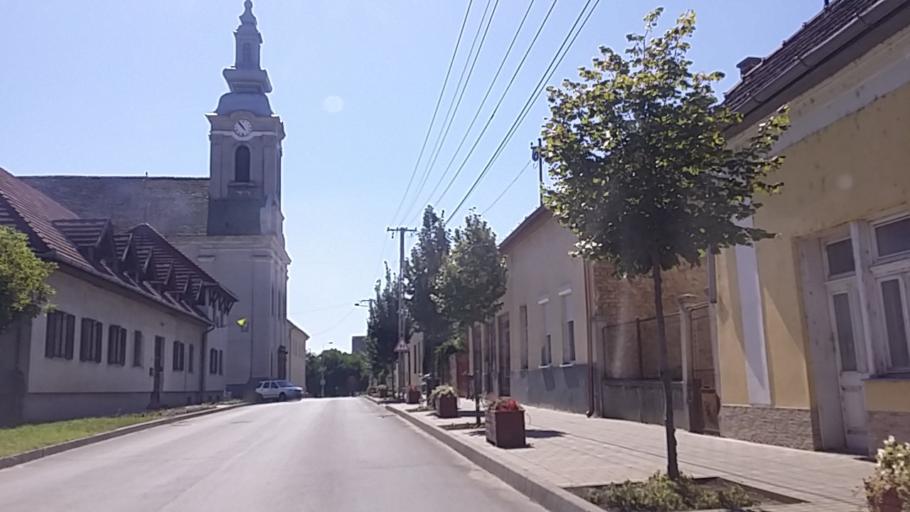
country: HU
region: Tolna
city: Simontornya
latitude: 46.7535
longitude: 18.5530
